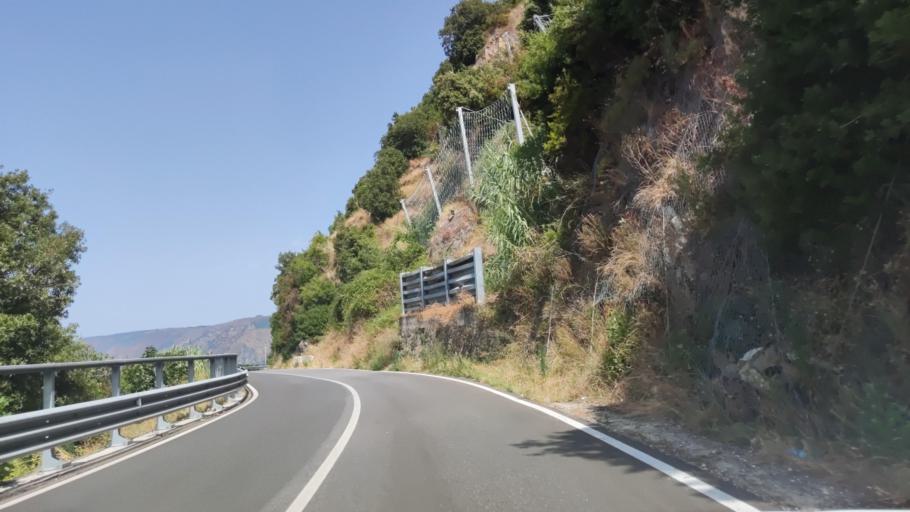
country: IT
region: Calabria
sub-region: Provincia di Reggio Calabria
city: Bagnara Calabra
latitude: 38.2733
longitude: 15.7834
